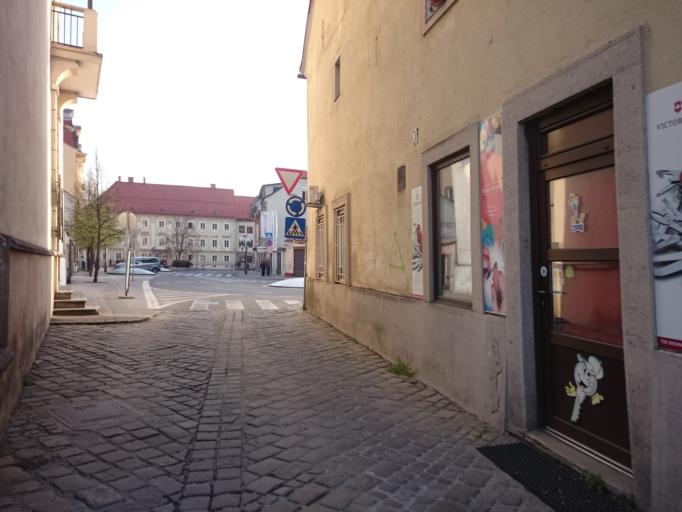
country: SI
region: Celje
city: Celje
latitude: 46.2285
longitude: 15.2611
